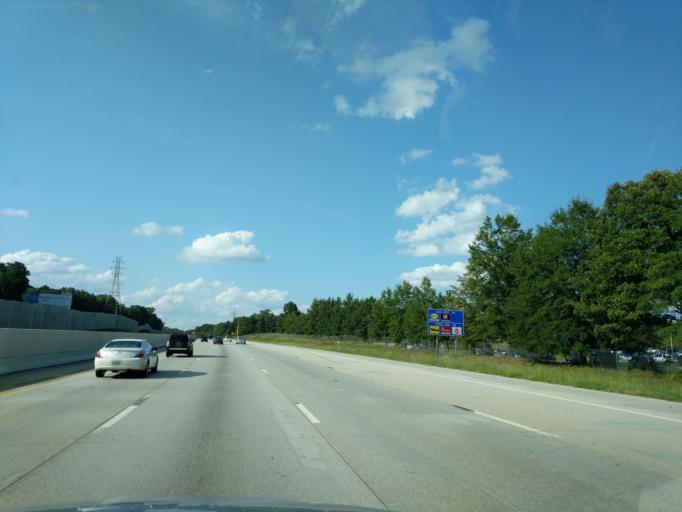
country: US
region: South Carolina
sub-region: Greenville County
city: Mauldin
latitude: 34.7949
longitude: -82.2800
